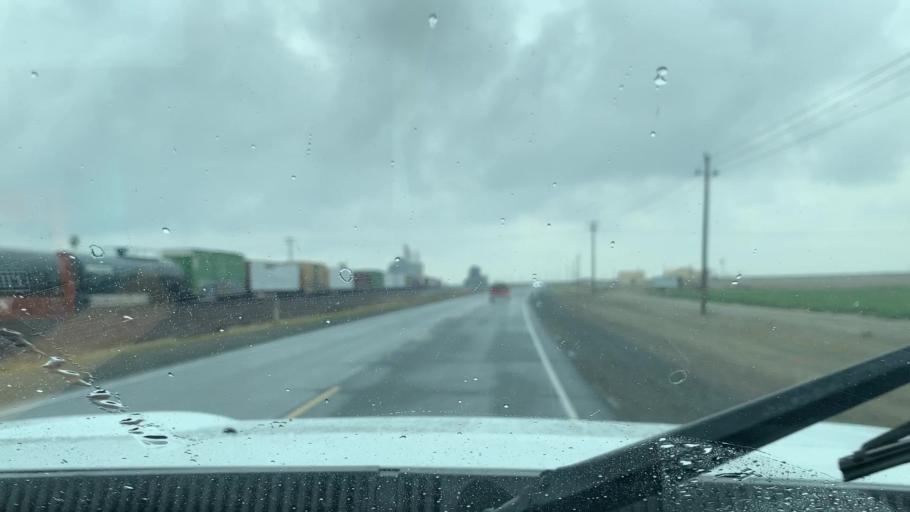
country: US
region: California
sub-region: Tulare County
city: Alpaugh
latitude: 35.9844
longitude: -119.4731
